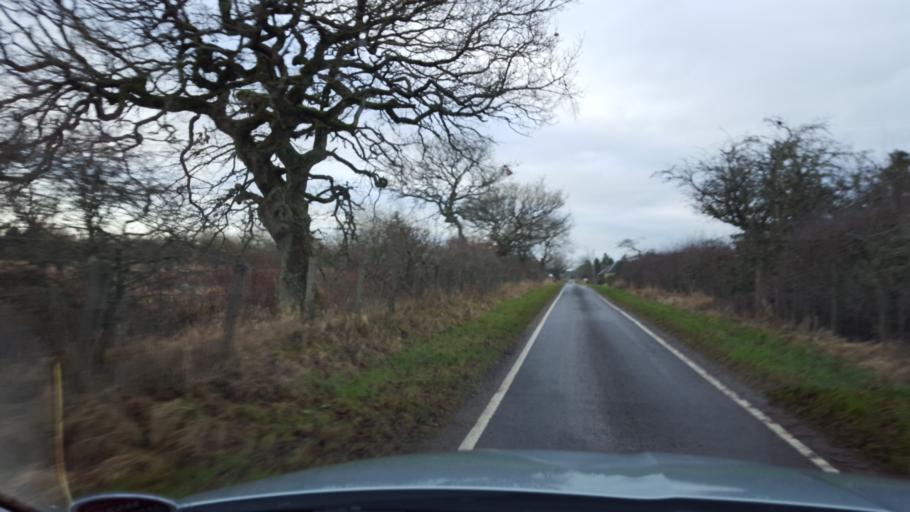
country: GB
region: Scotland
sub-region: West Lothian
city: Mid Calder
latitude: 55.8397
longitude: -3.5030
